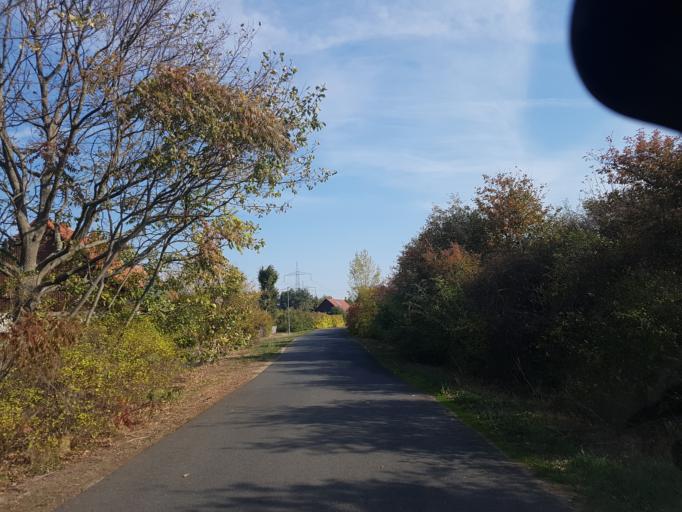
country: DE
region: Brandenburg
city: Ihlow
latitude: 51.8357
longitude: 13.3127
